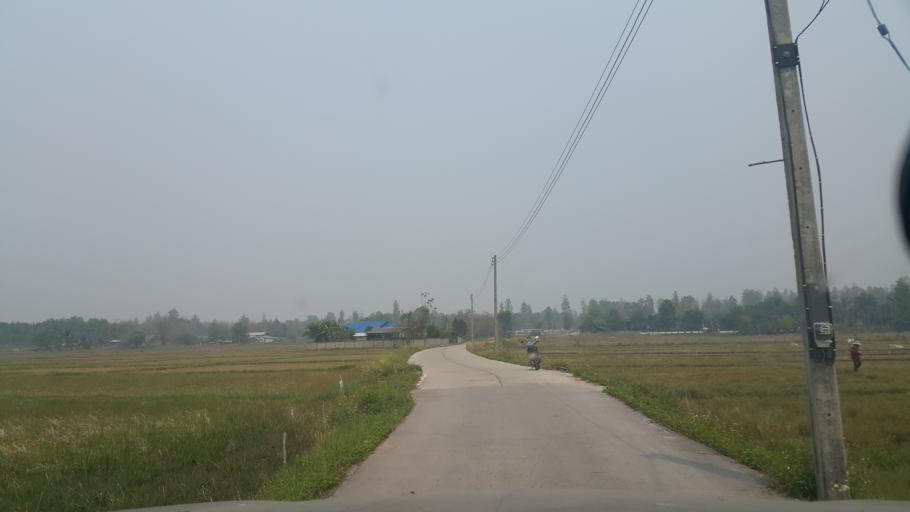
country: TH
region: Lampang
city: Hang Chat
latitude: 18.2744
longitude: 99.2604
